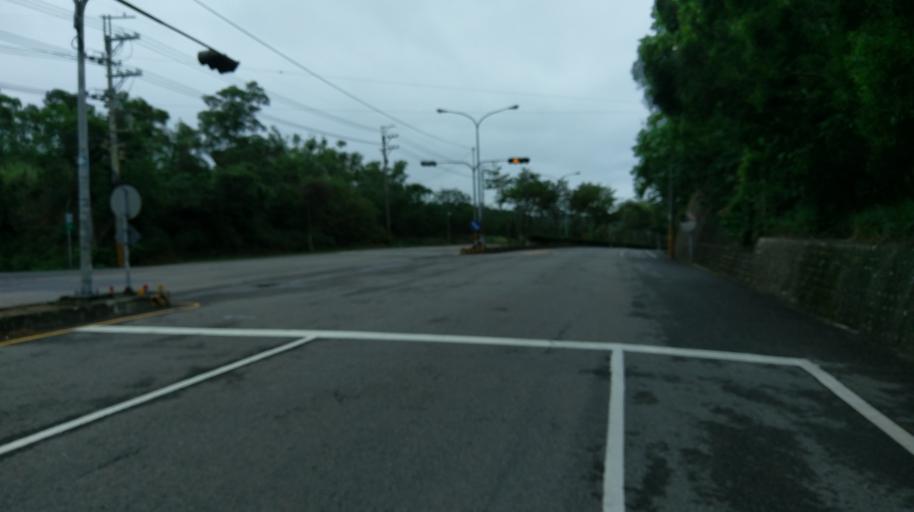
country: TW
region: Taiwan
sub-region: Miaoli
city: Miaoli
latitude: 24.6432
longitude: 120.8451
